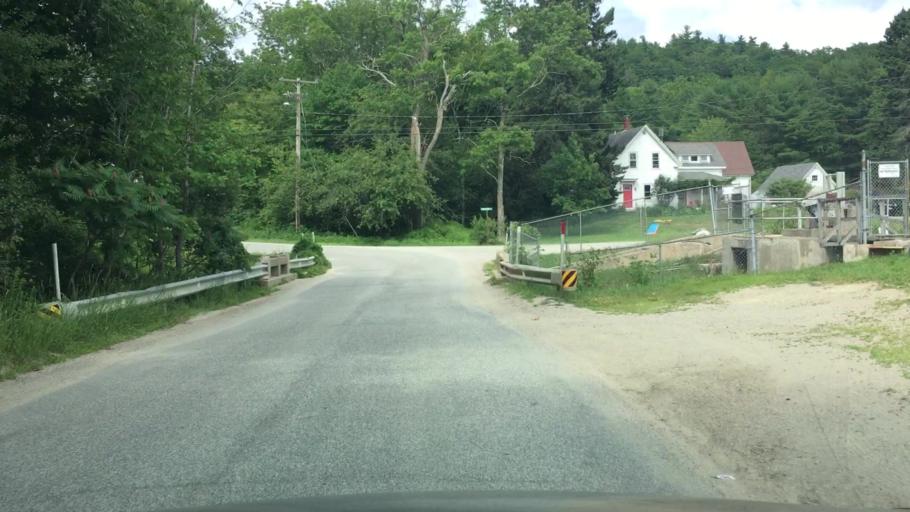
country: US
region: Maine
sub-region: Hancock County
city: Orland
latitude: 44.5680
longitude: -68.6784
